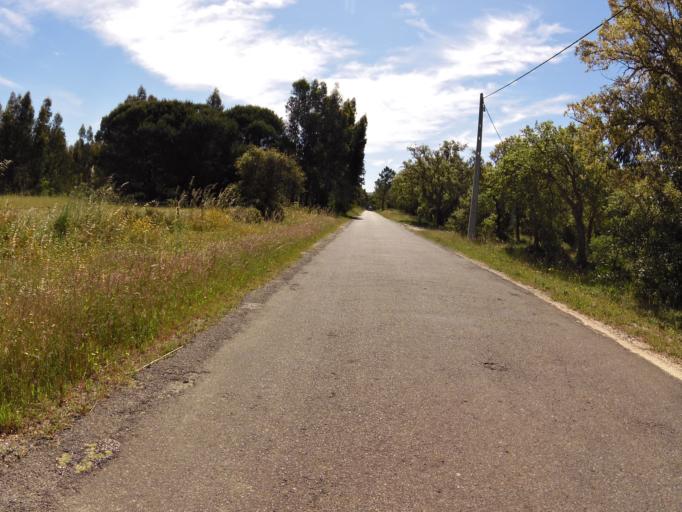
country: PT
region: Setubal
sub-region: Sines
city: Porto Covo
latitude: 37.9369
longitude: -8.7667
